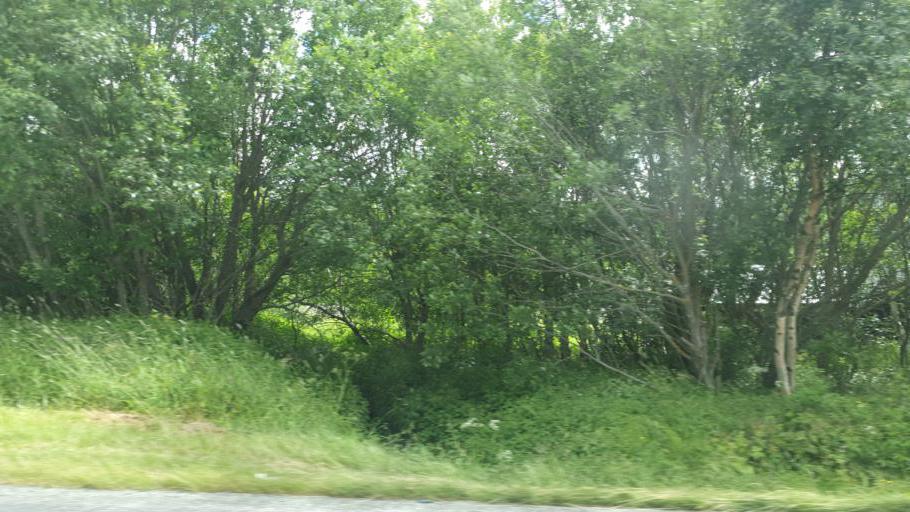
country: NO
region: Sor-Trondelag
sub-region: Oppdal
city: Oppdal
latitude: 62.6081
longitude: 9.7389
